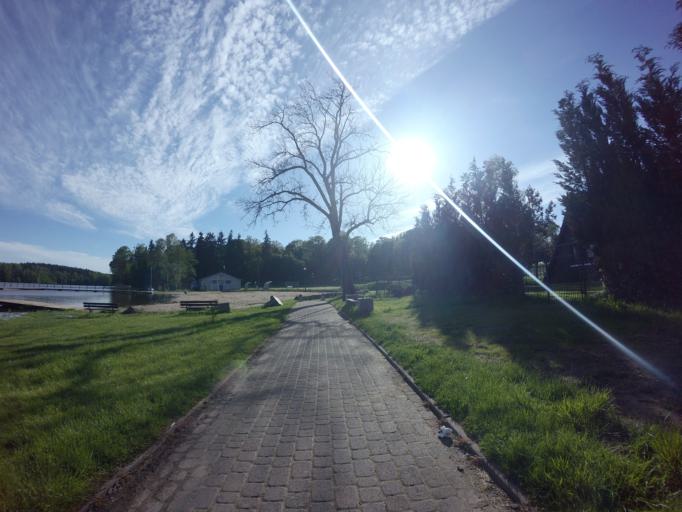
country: PL
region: West Pomeranian Voivodeship
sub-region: Powiat choszczenski
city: Drawno
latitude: 53.2140
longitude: 15.7498
